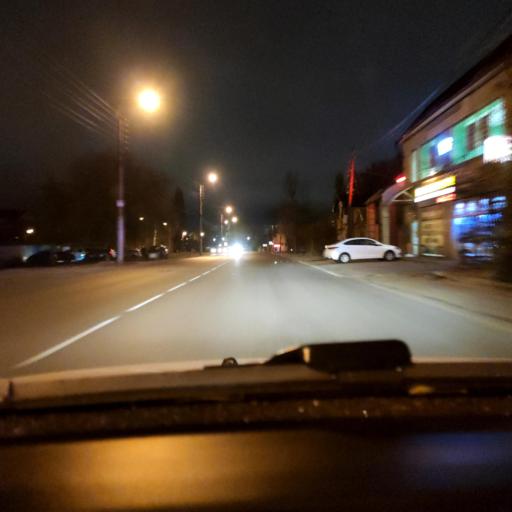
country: RU
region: Voronezj
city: Voronezh
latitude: 51.6305
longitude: 39.1751
